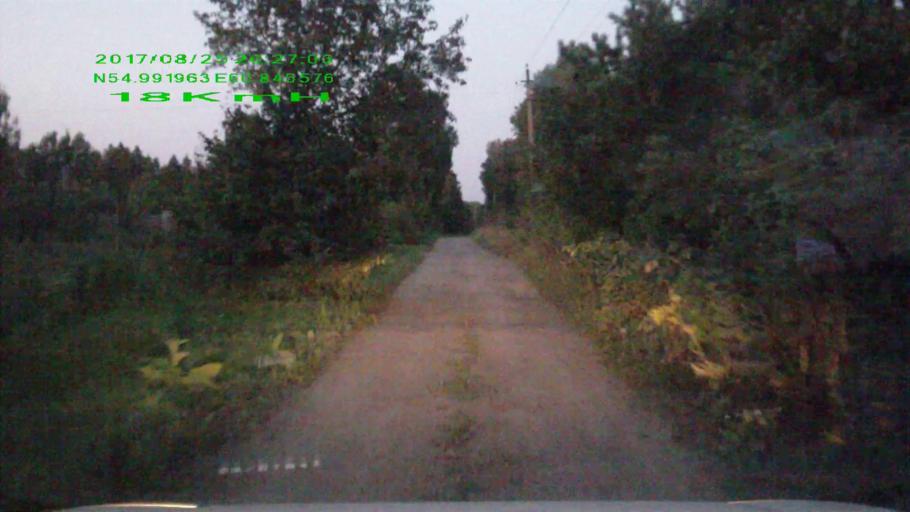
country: RU
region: Chelyabinsk
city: Timiryazevskiy
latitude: 54.9925
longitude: 60.8468
